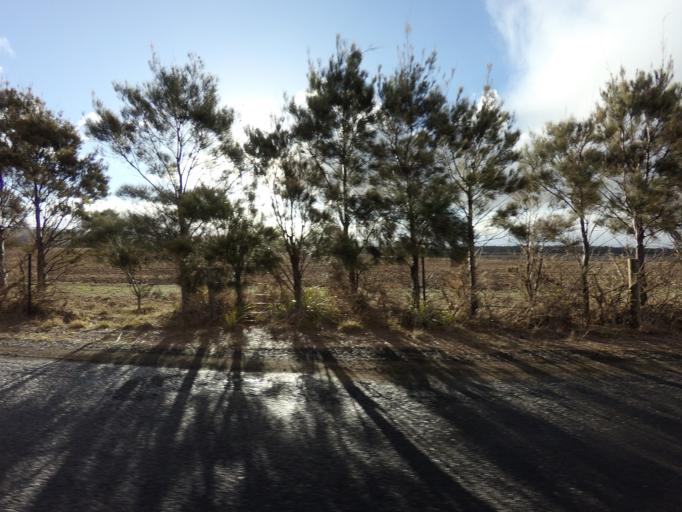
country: AU
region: Tasmania
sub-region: Break O'Day
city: St Helens
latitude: -42.0959
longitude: 148.0700
